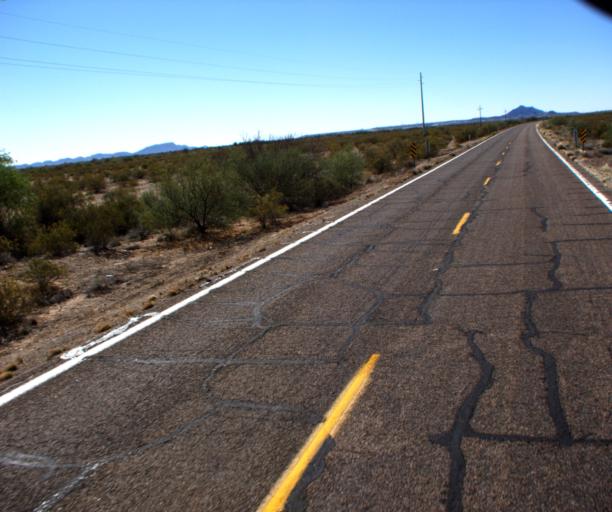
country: US
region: Arizona
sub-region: Pima County
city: Ajo
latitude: 32.4586
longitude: -112.8726
